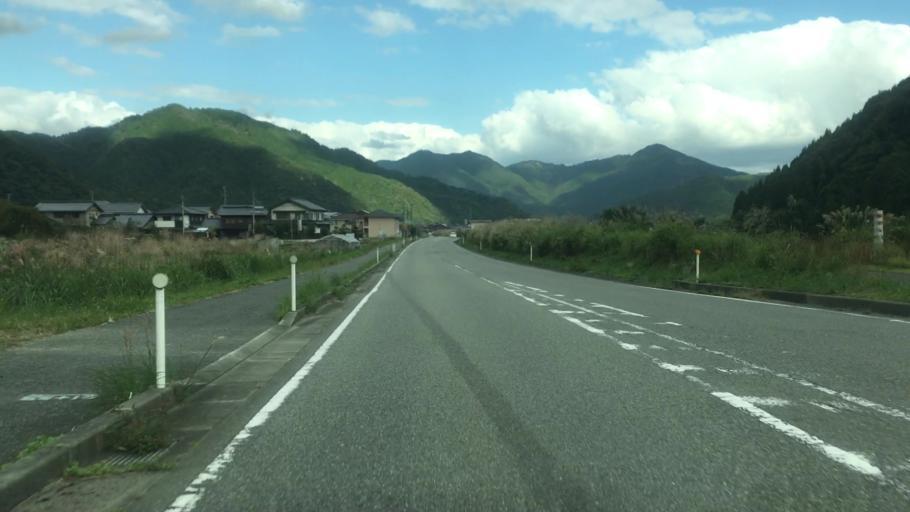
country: JP
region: Hyogo
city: Toyooka
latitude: 35.3724
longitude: 134.7653
